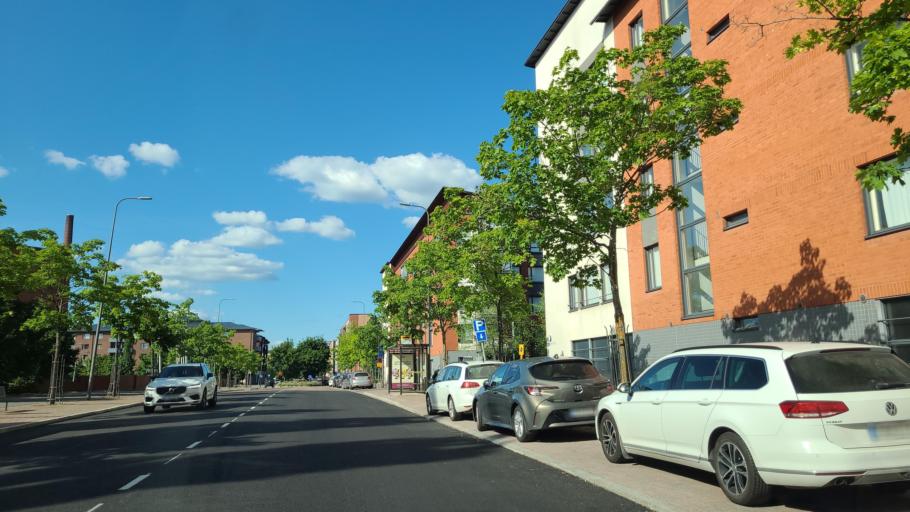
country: FI
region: Central Finland
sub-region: Jyvaeskylae
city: Jyvaeskylae
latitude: 62.2383
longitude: 25.7606
